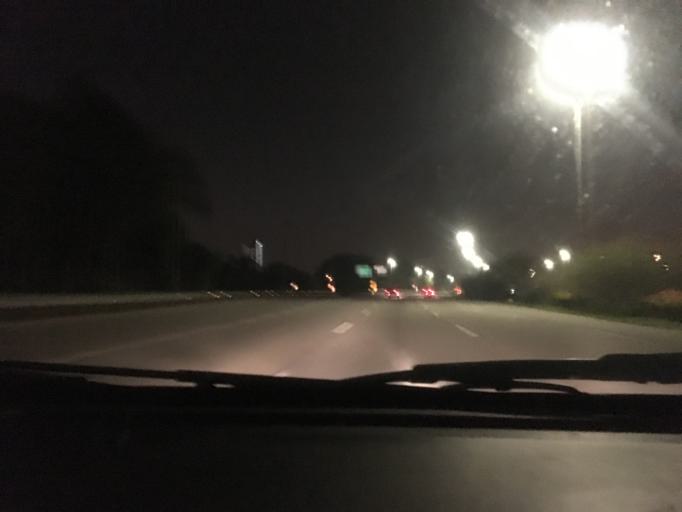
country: MY
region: Putrajaya
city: Putrajaya
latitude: 2.9232
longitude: 101.6648
